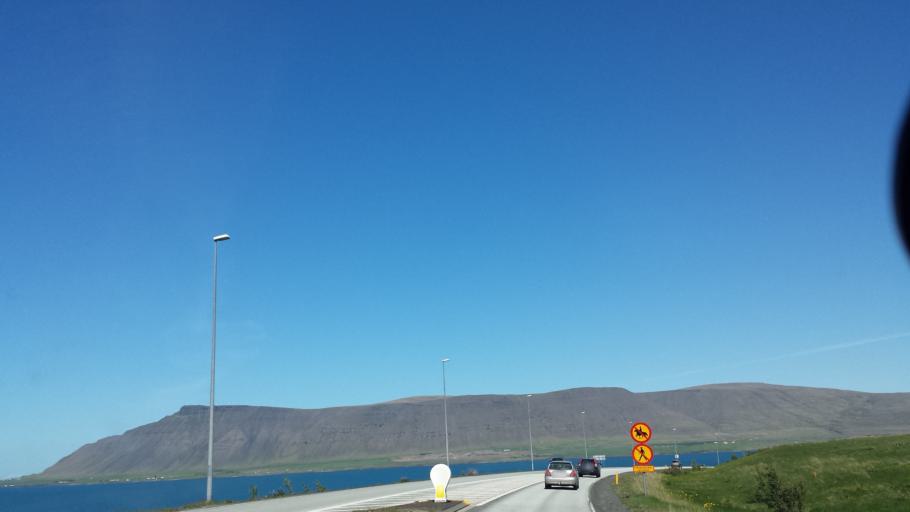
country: IS
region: Capital Region
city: Reykjavik
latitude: 64.2750
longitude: -21.8393
